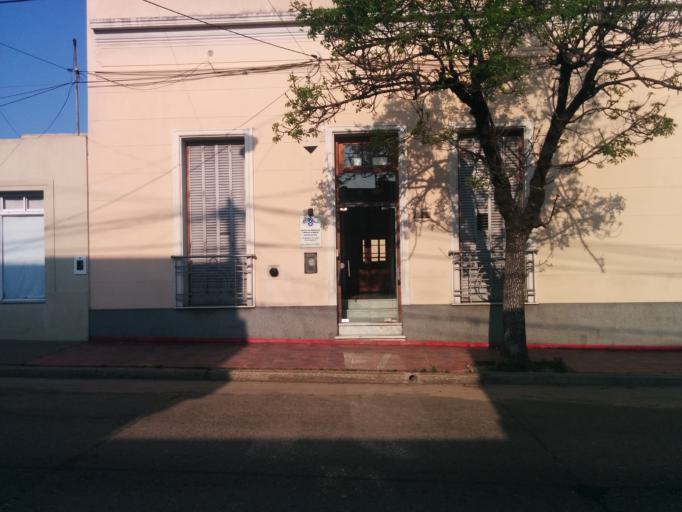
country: AR
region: Entre Rios
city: Concordia
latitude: -31.3874
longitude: -58.0187
